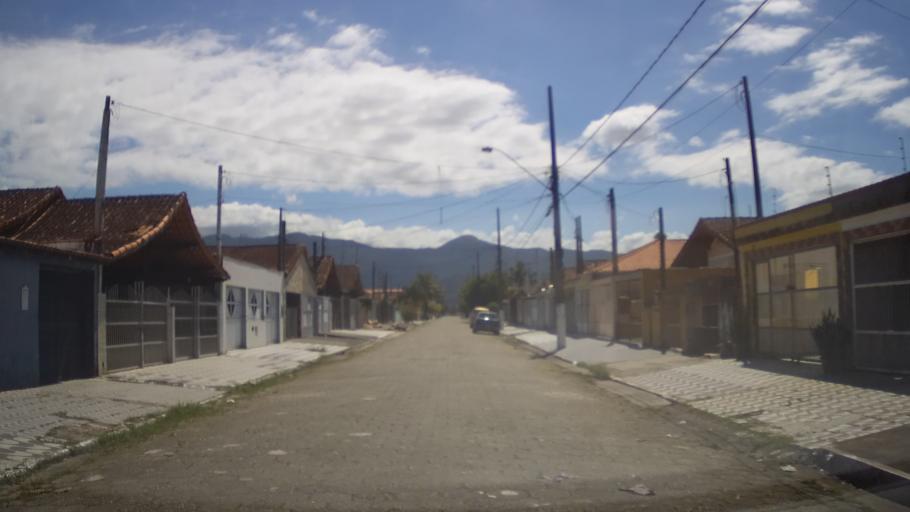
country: BR
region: Sao Paulo
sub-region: Praia Grande
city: Praia Grande
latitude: -24.0390
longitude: -46.5056
